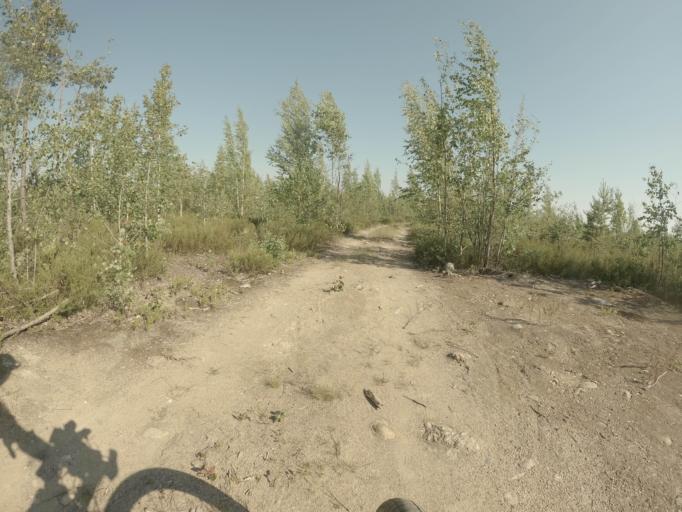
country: RU
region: Leningrad
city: Yakovlevo
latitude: 60.4432
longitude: 29.2404
